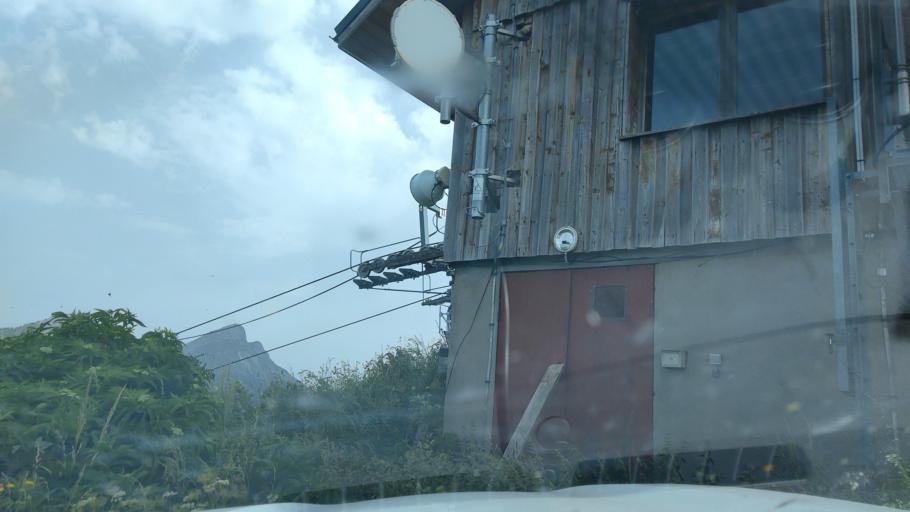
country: FR
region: Rhone-Alpes
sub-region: Departement de la Savoie
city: Cruet
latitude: 45.5941
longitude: 6.1135
